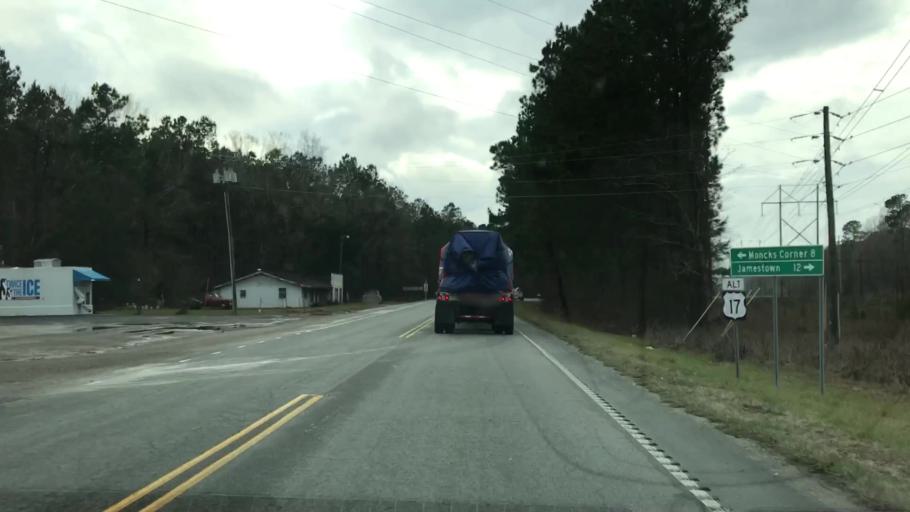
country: US
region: South Carolina
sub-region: Berkeley County
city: Bonneau Beach
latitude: 33.2706
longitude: -79.8988
